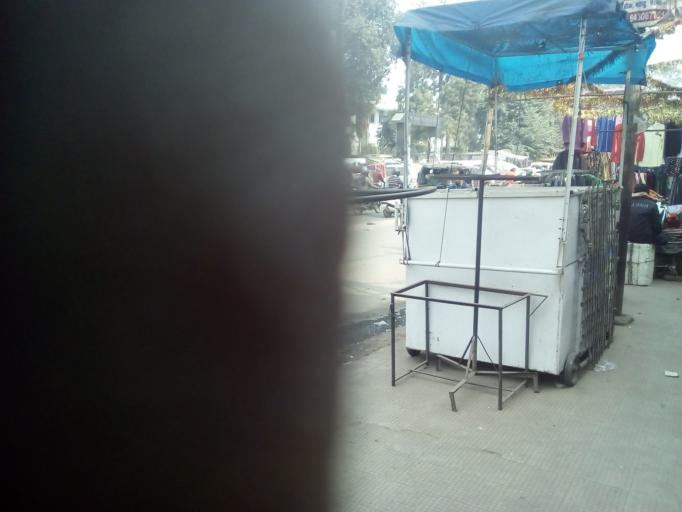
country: IN
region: Bihar
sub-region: Patna
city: Patna
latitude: 25.6197
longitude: 85.1560
